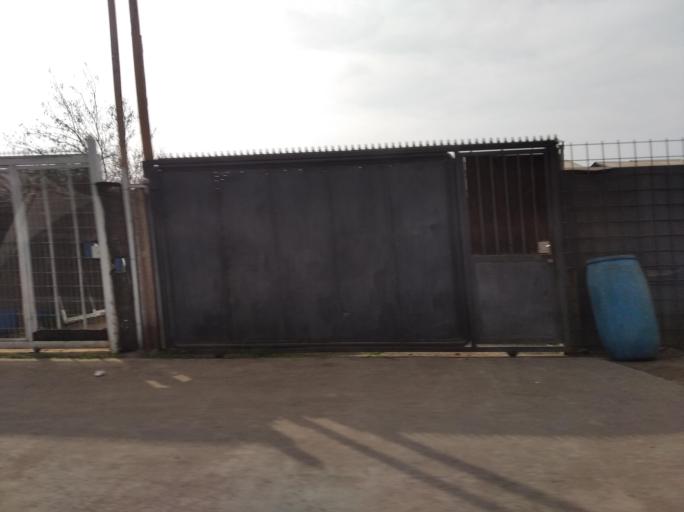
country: CL
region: Santiago Metropolitan
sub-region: Provincia de Chacabuco
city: Lampa
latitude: -33.2859
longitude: -70.8874
